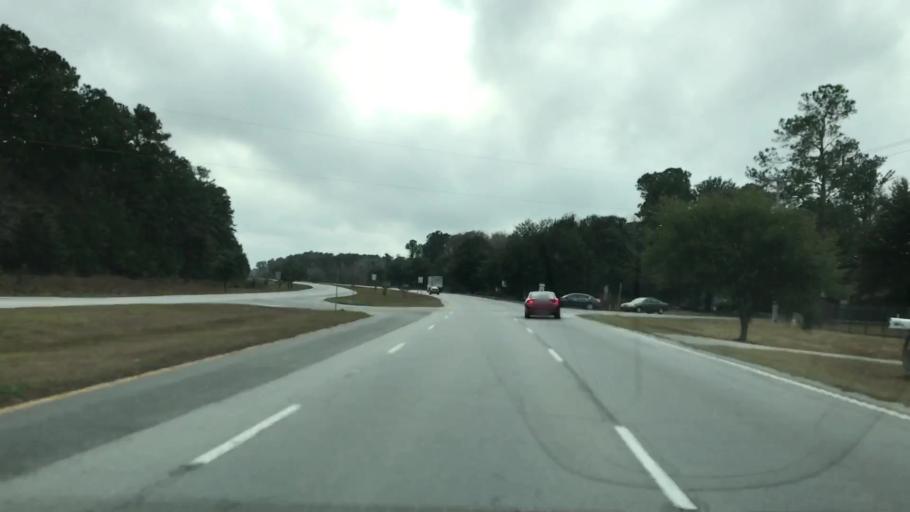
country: US
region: South Carolina
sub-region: Berkeley County
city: Moncks Corner
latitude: 33.1831
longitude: -80.0160
